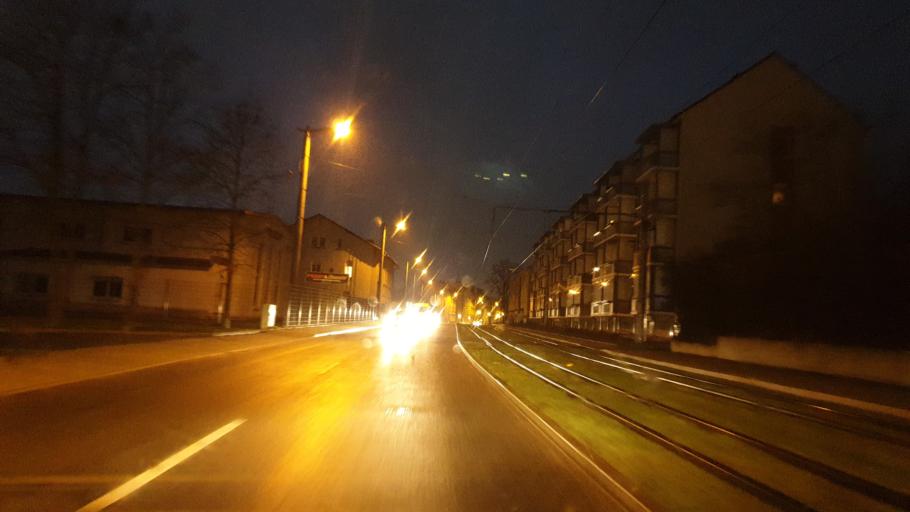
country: DE
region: Thuringia
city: Gera
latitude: 50.8978
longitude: 12.0753
